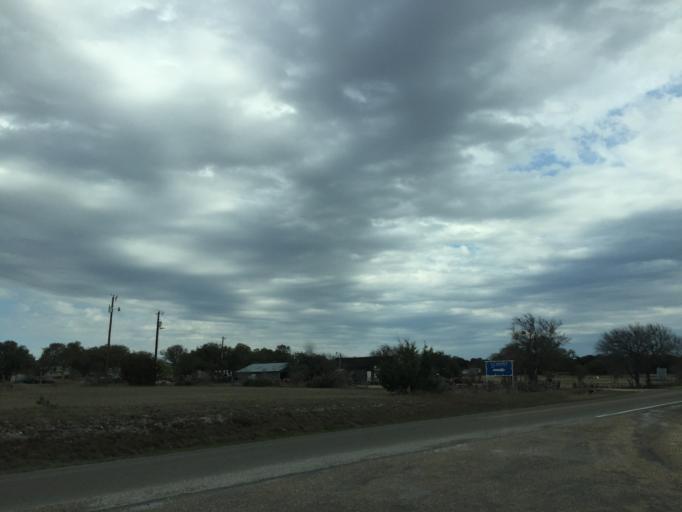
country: US
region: Texas
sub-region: Burnet County
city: Bertram
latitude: 30.6546
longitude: -98.0150
